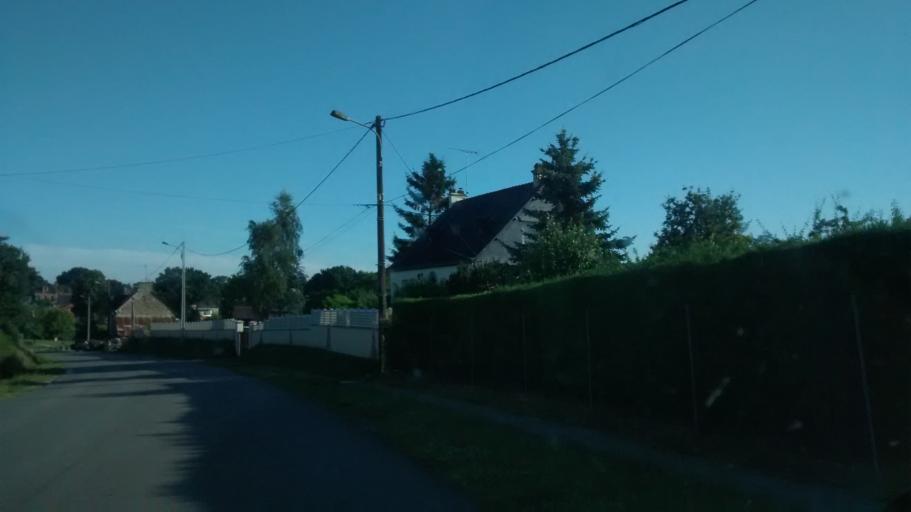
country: FR
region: Brittany
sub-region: Departement du Morbihan
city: Campeneac
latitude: 47.9543
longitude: -2.2899
